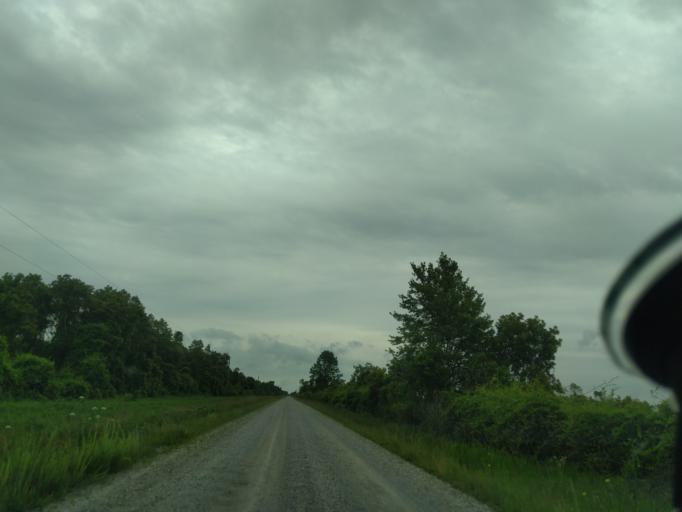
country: US
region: North Carolina
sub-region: Beaufort County
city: Belhaven
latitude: 35.7439
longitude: -76.4882
